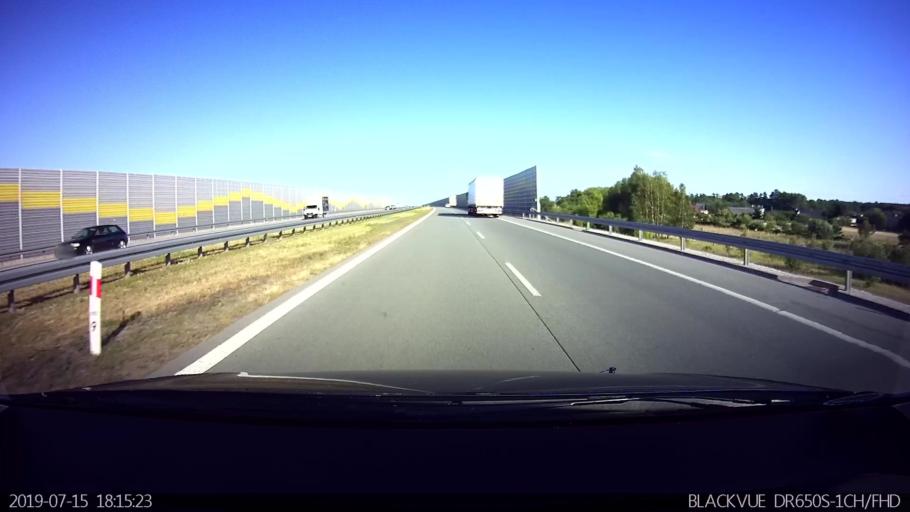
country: PL
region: Lodz Voivodeship
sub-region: Powiat zdunskowolski
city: Zdunska Wola
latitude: 51.5807
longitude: 18.9084
